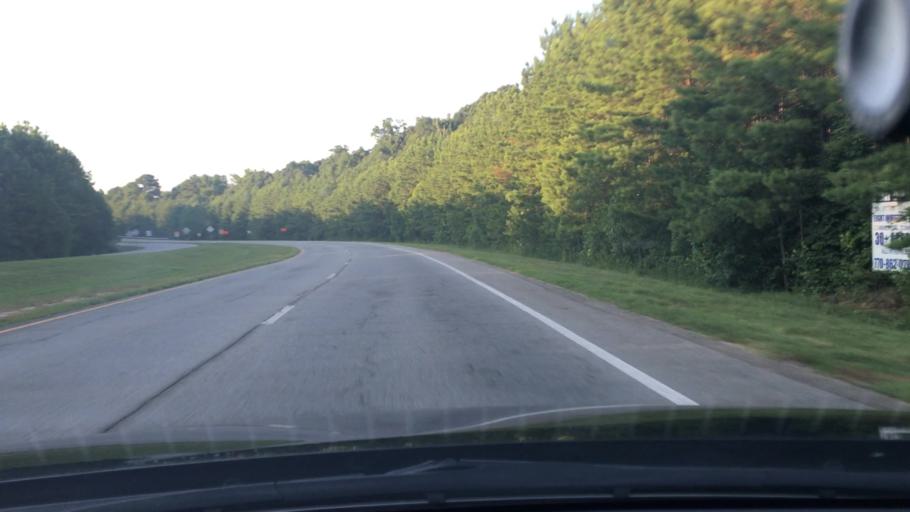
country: US
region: Georgia
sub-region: Coweta County
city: East Newnan
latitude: 33.3689
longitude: -84.7632
